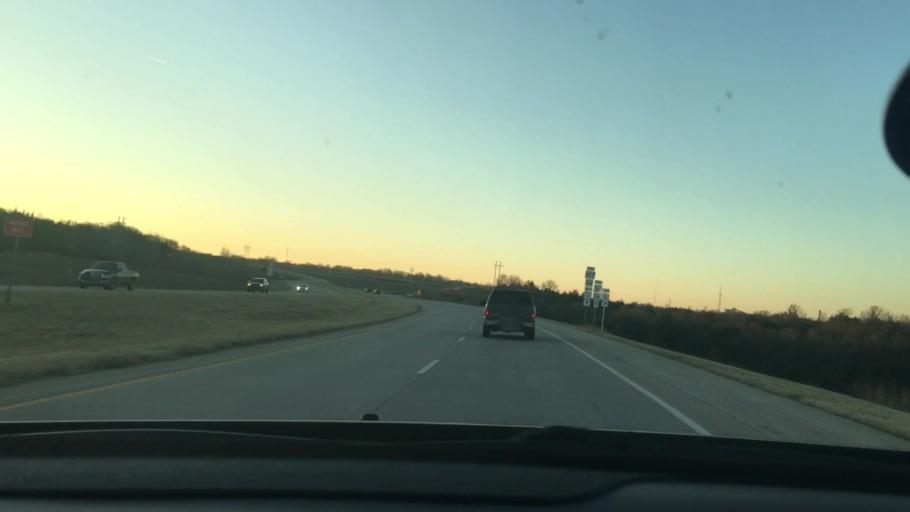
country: US
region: Oklahoma
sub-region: Pontotoc County
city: Ada
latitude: 34.7970
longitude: -96.6956
